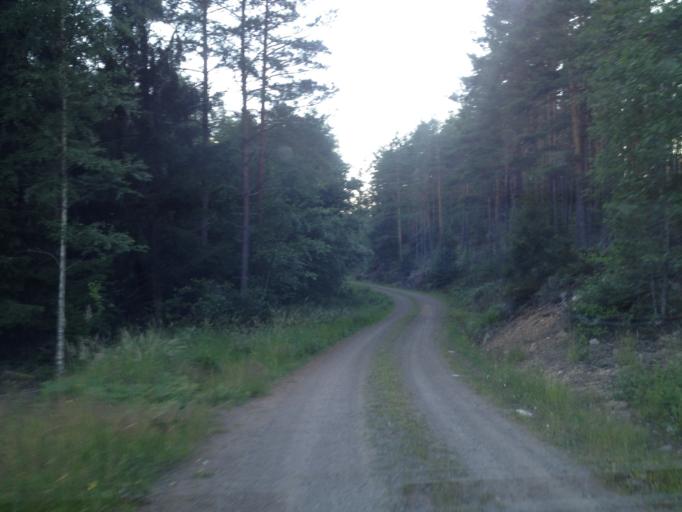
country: SE
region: Kalmar
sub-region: Vasterviks Kommun
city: Overum
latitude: 57.9977
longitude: 16.1396
